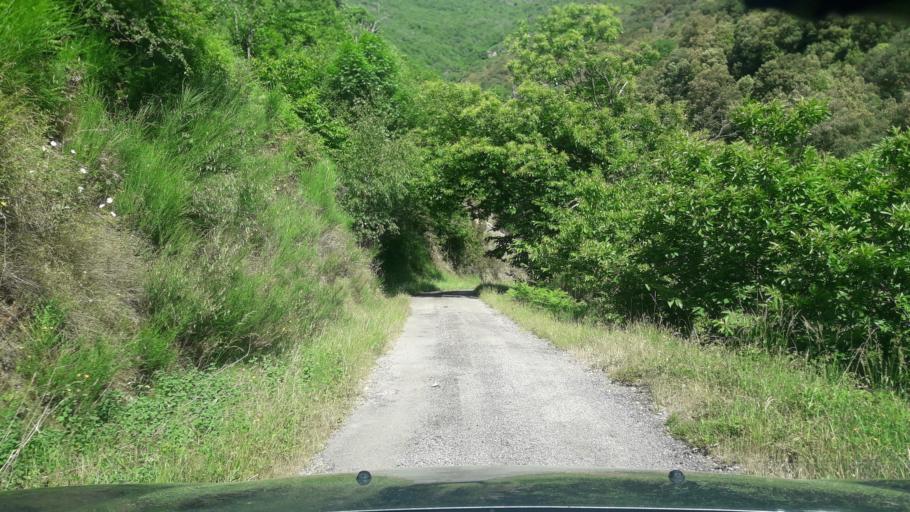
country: FR
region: Languedoc-Roussillon
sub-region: Departement du Gard
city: Valleraugue
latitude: 44.1099
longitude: 3.6936
